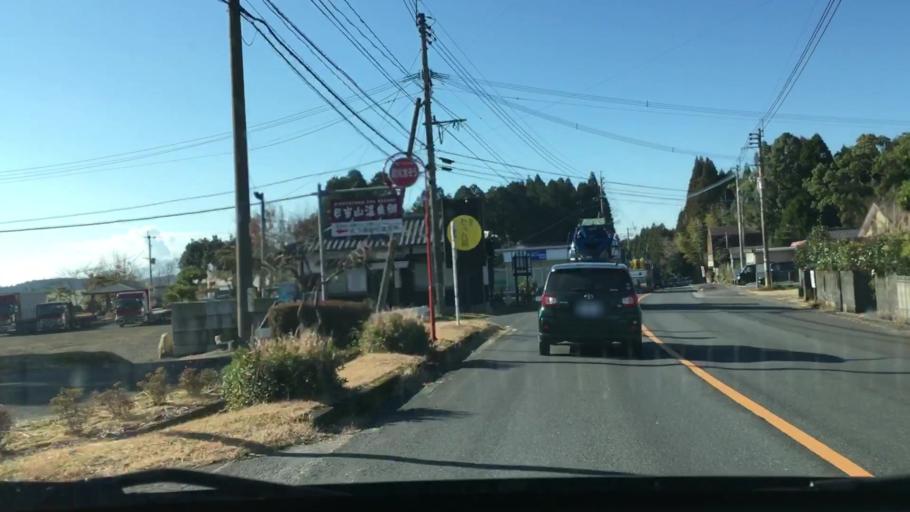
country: JP
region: Kagoshima
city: Kajiki
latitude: 31.7777
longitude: 130.7025
